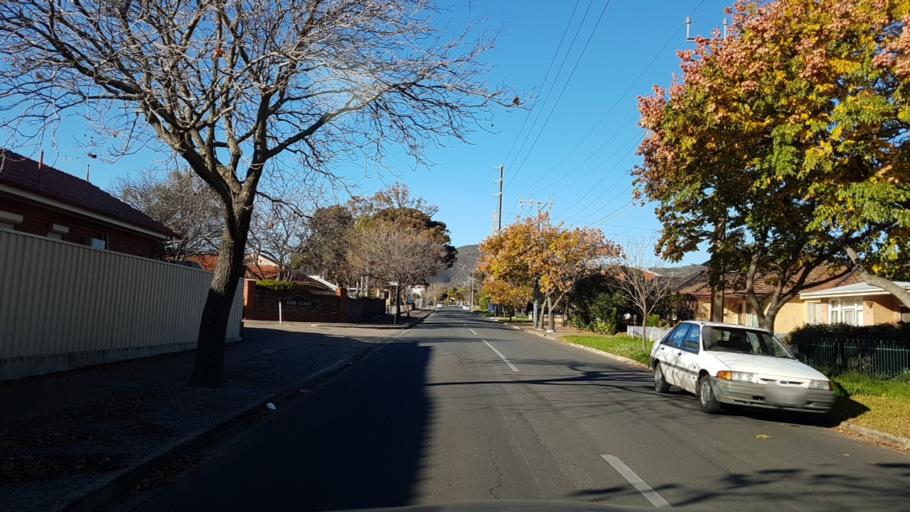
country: AU
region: South Australia
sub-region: Campbelltown
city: Campbelltown
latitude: -34.8846
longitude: 138.6794
